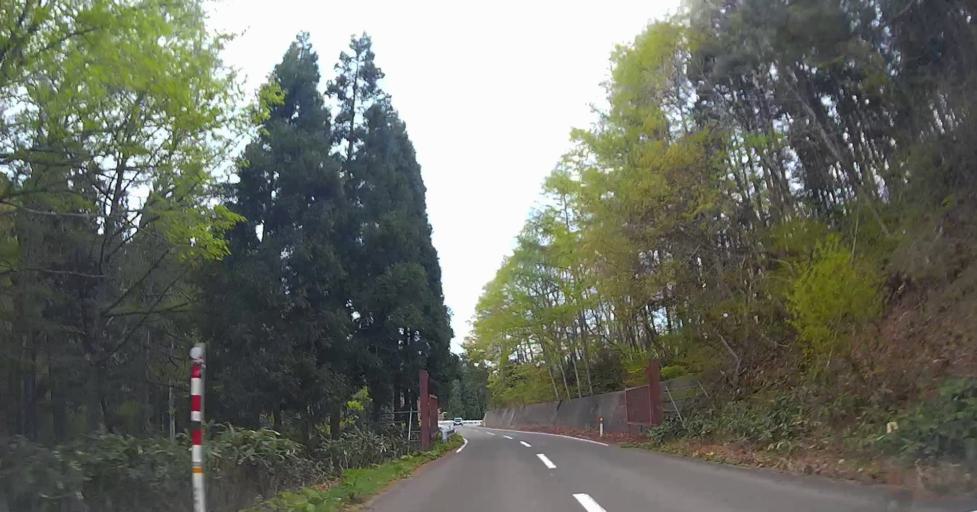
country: JP
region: Aomori
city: Goshogawara
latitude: 40.9022
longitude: 140.4995
